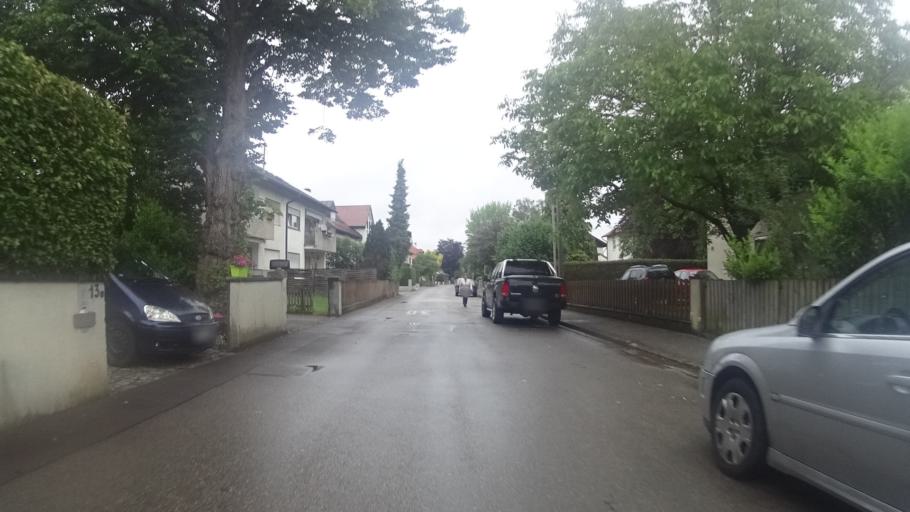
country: DE
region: Bavaria
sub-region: Upper Bavaria
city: Mammendorf
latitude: 48.2115
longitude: 11.1657
